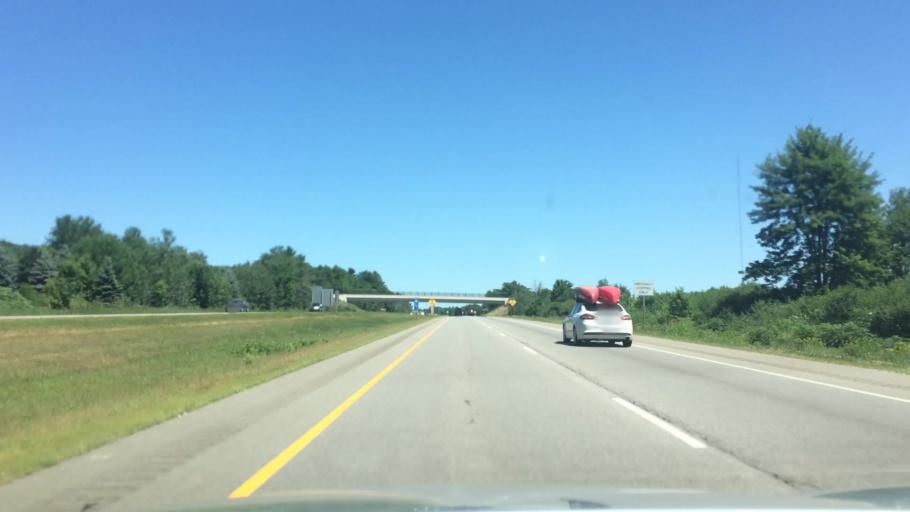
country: US
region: Wisconsin
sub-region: Marathon County
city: Rothschild
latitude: 44.8769
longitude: -89.6436
